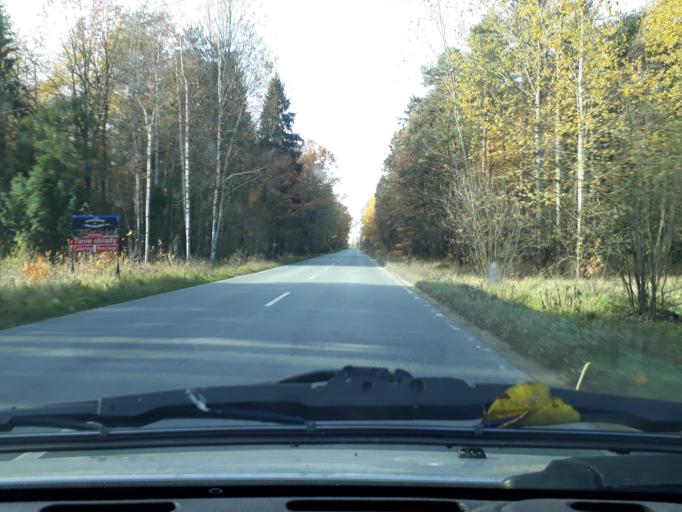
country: PL
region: Silesian Voivodeship
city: Wozniki
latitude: 50.5762
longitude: 19.0127
